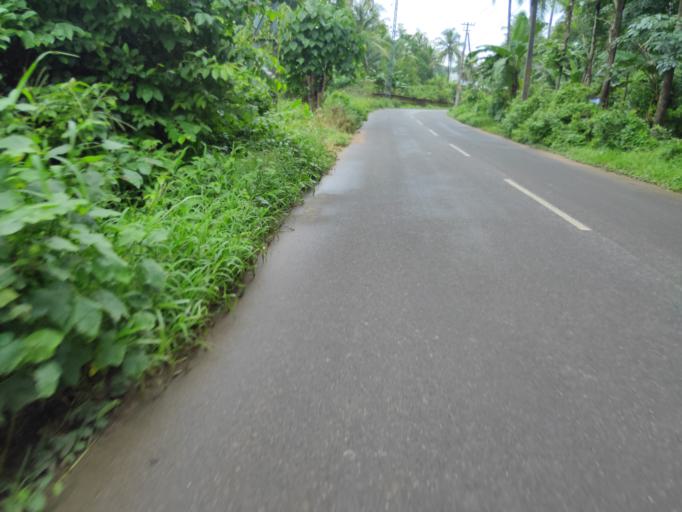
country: IN
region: Kerala
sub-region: Malappuram
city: Manjeri
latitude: 11.2269
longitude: 76.2731
